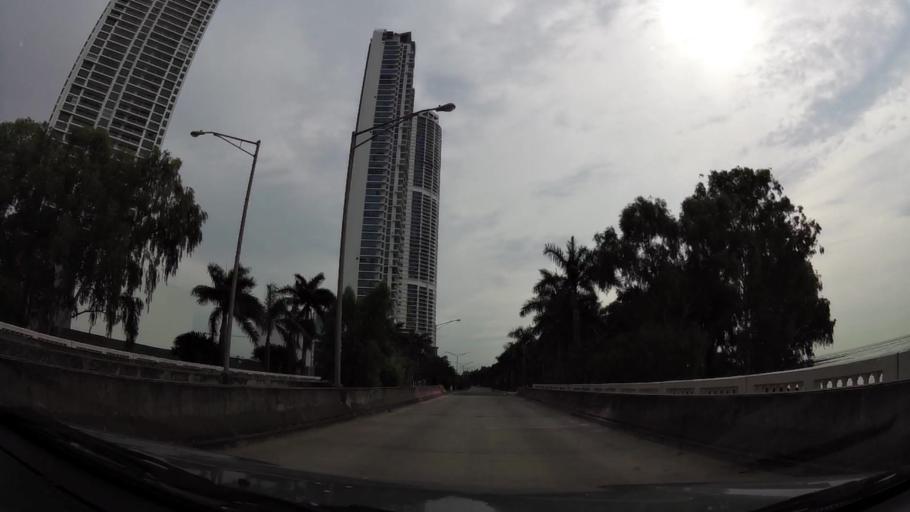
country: PA
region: Panama
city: San Miguelito
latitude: 9.0096
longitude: -79.4689
